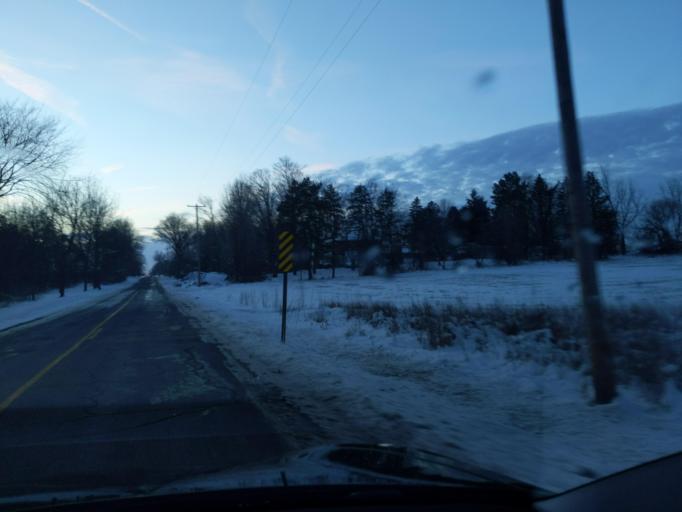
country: US
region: Michigan
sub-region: Ingham County
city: Mason
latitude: 42.5819
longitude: -84.3767
